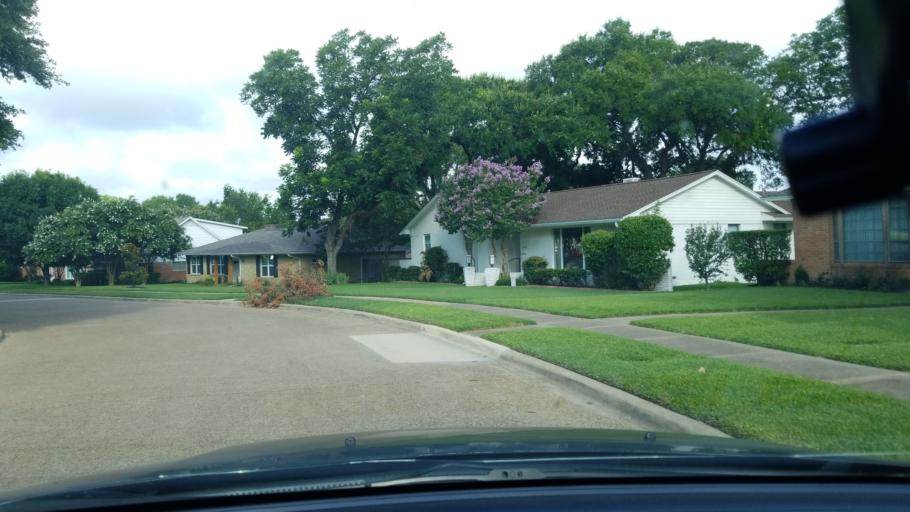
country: US
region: Texas
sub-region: Dallas County
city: Highland Park
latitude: 32.8210
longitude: -96.6890
